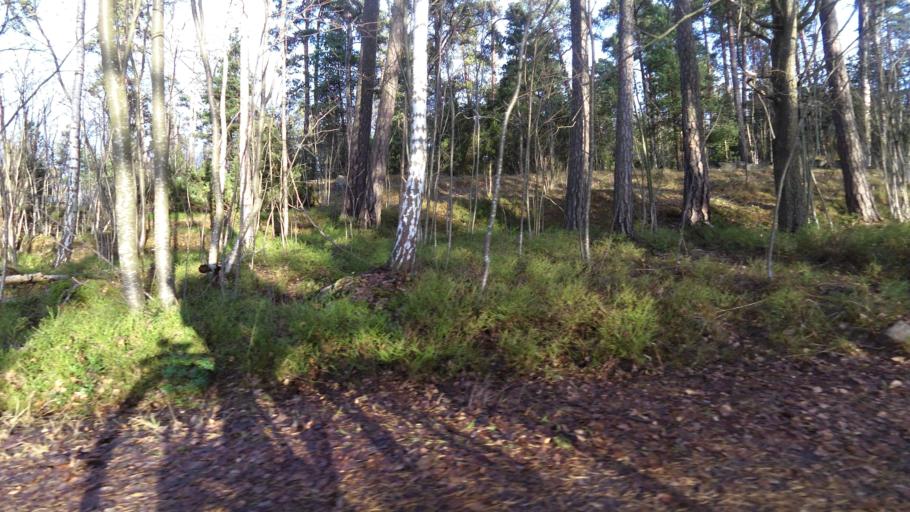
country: FI
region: Uusimaa
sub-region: Helsinki
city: Otaniemi
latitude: 60.1675
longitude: 24.8256
